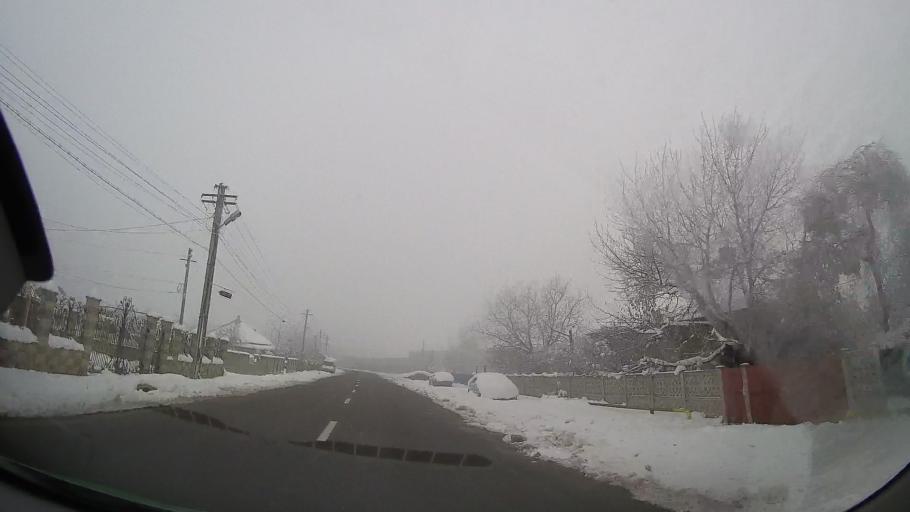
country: RO
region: Iasi
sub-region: Municipiul Pascani
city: Pascani
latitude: 47.2378
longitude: 26.7281
